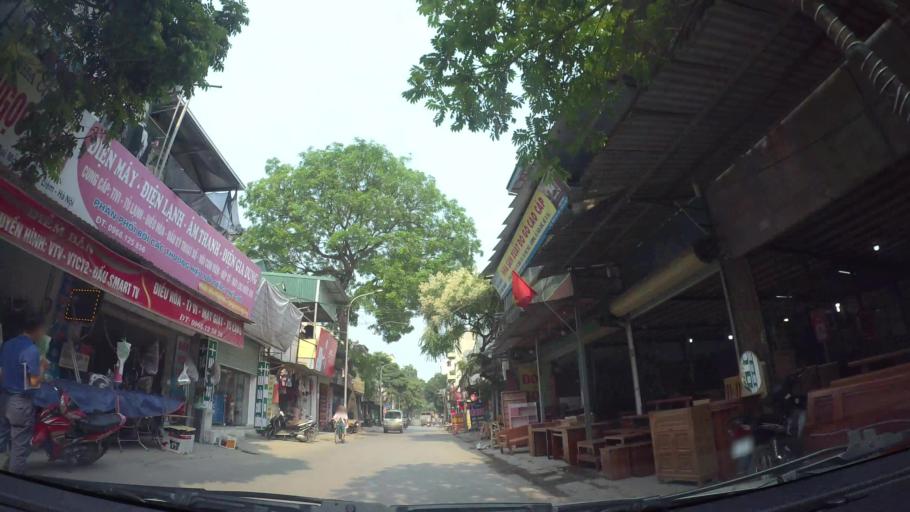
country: VN
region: Ha Noi
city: Ha Dong
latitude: 20.9957
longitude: 105.7537
